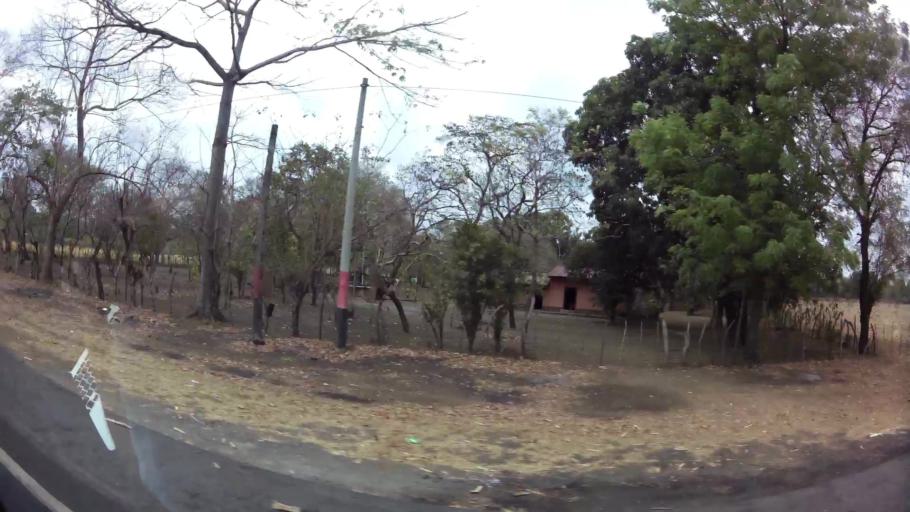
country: NI
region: Leon
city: Telica
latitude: 12.5195
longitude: -86.8668
